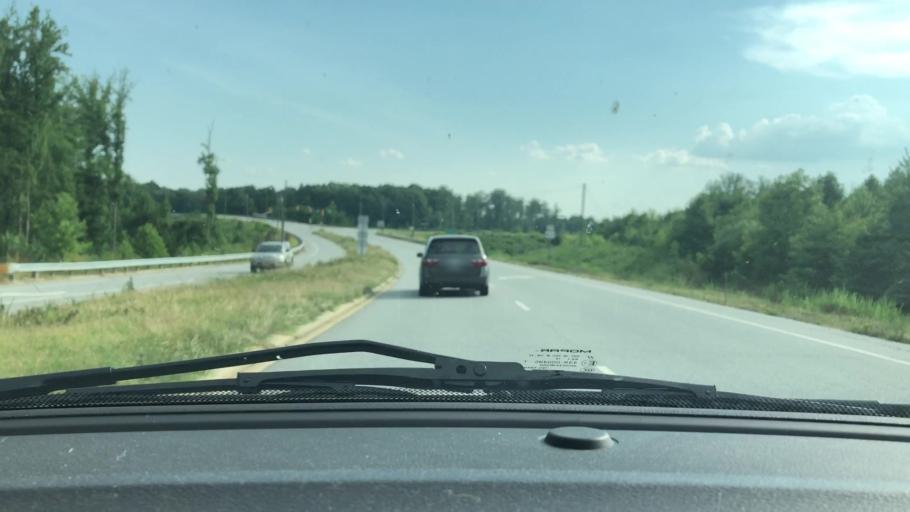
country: US
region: North Carolina
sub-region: Guilford County
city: Forest Oaks
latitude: 35.9668
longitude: -79.7020
